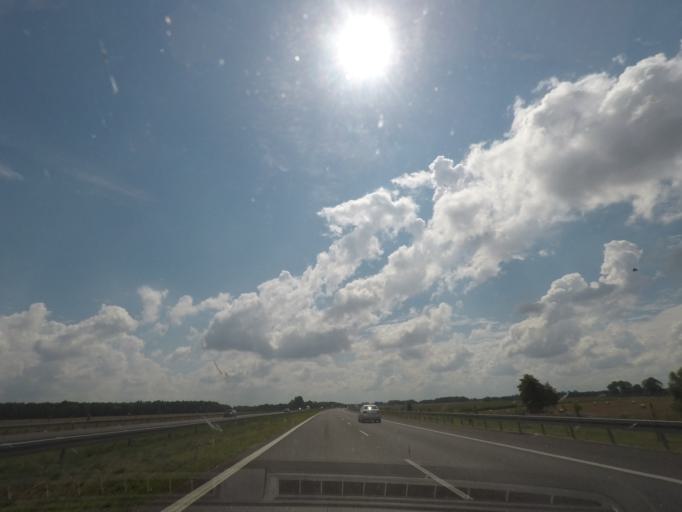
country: PL
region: Lodz Voivodeship
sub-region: Powiat zgierski
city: Strykow
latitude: 51.9538
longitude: 19.5999
